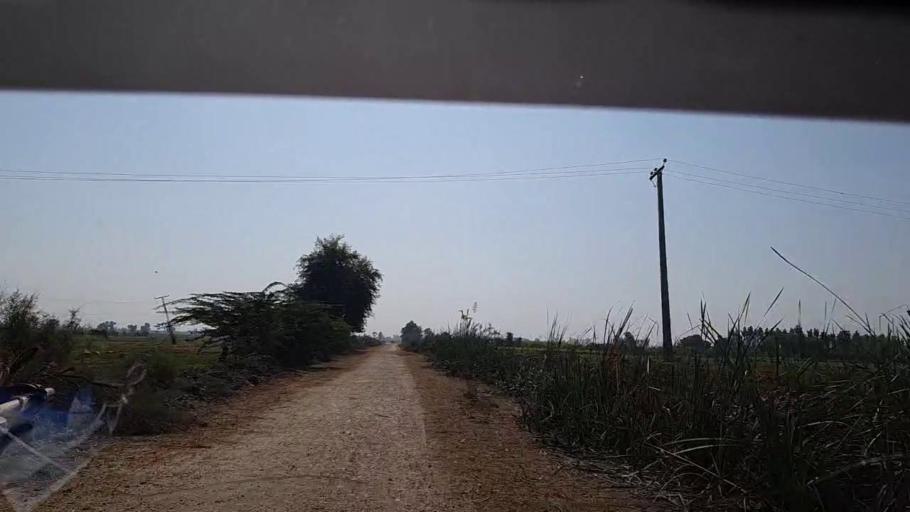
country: PK
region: Sindh
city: Naudero
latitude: 27.6962
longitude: 68.4022
